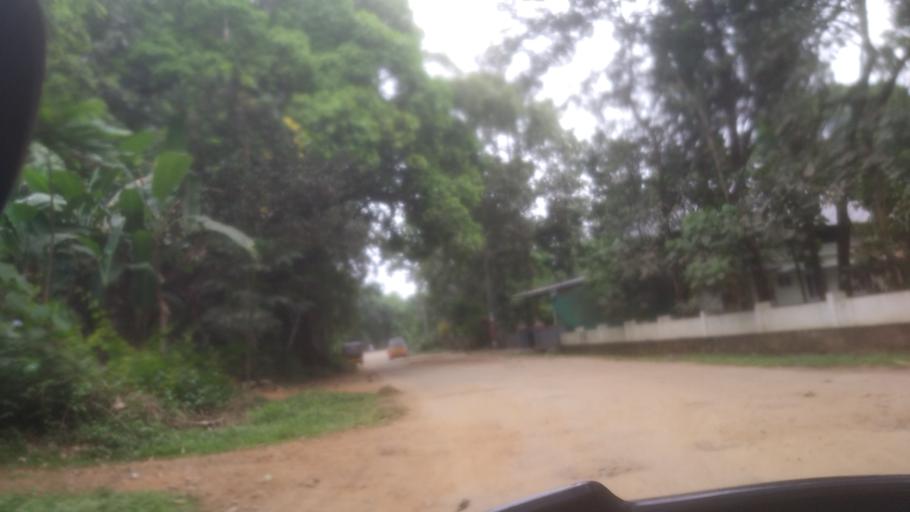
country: IN
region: Kerala
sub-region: Ernakulam
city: Perumbavoor
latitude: 10.0485
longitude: 76.5256
